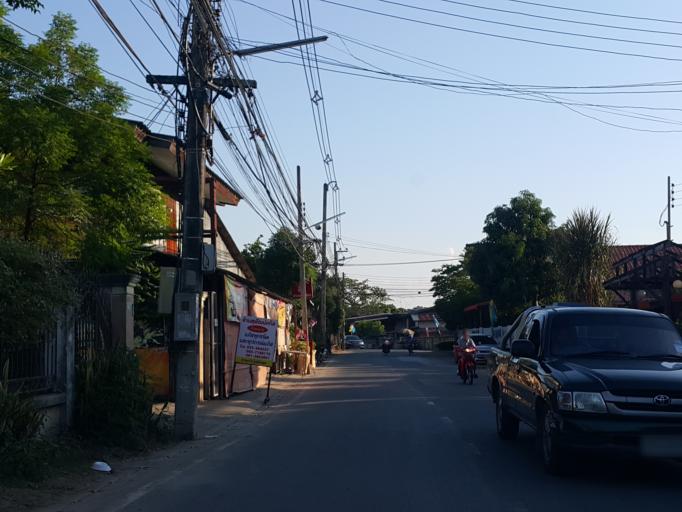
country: TH
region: Chiang Mai
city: San Sai
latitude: 18.7850
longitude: 99.0501
